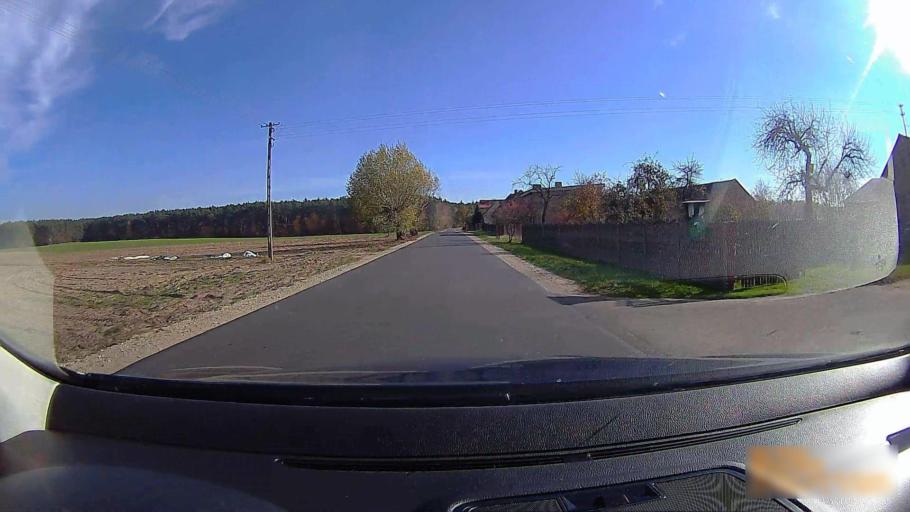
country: PL
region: Greater Poland Voivodeship
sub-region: Powiat ostrzeszowski
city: Ostrzeszow
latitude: 51.4116
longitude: 17.9872
